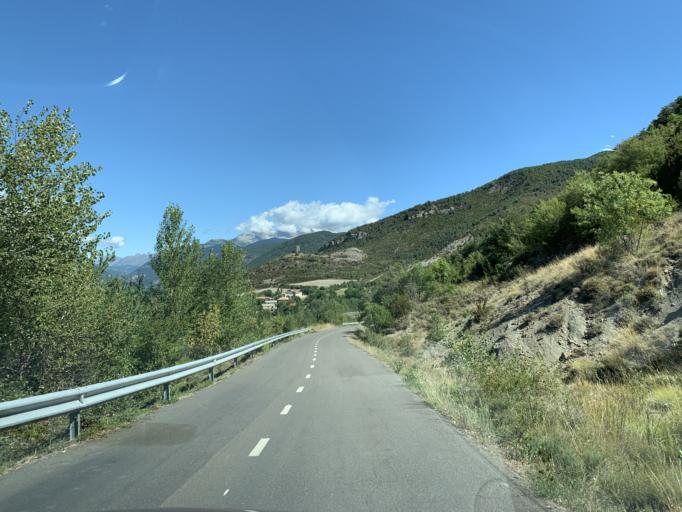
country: ES
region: Aragon
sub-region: Provincia de Huesca
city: Sabinanigo
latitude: 42.5472
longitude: -0.3186
